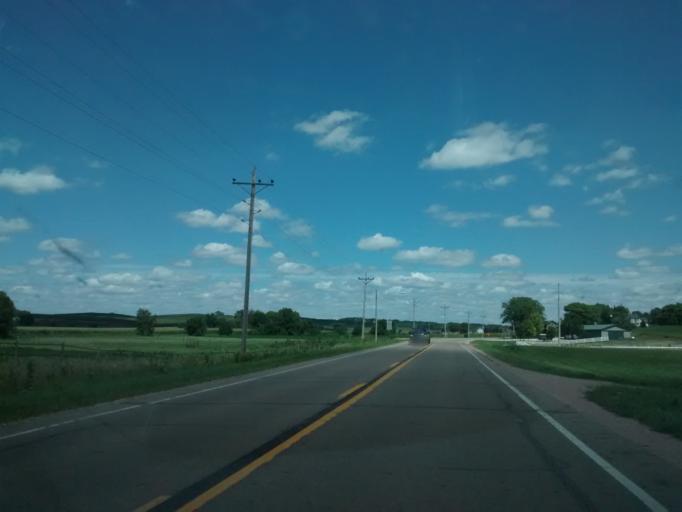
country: US
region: Iowa
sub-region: Woodbury County
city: Moville
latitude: 42.4954
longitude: -96.0720
